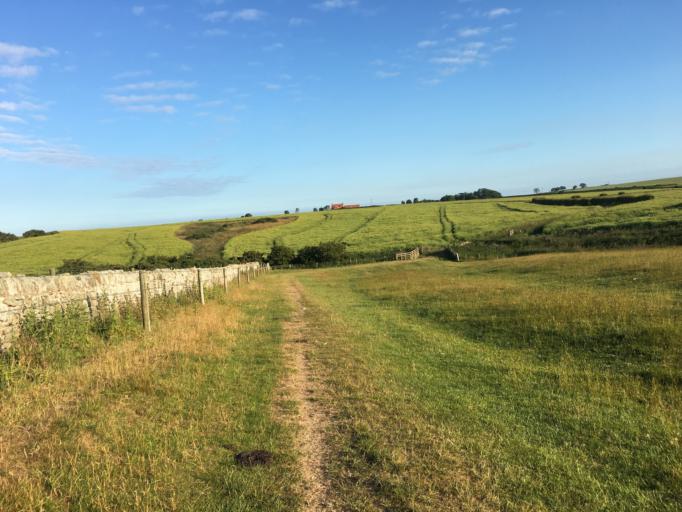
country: GB
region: England
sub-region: Northumberland
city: Bamburgh
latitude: 55.5970
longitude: -1.6940
